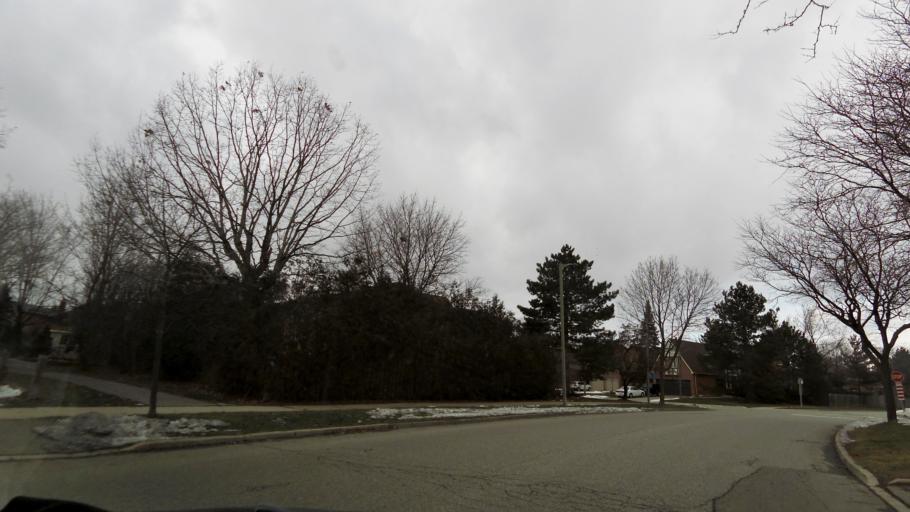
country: CA
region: Ontario
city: Mississauga
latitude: 43.5543
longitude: -79.6909
